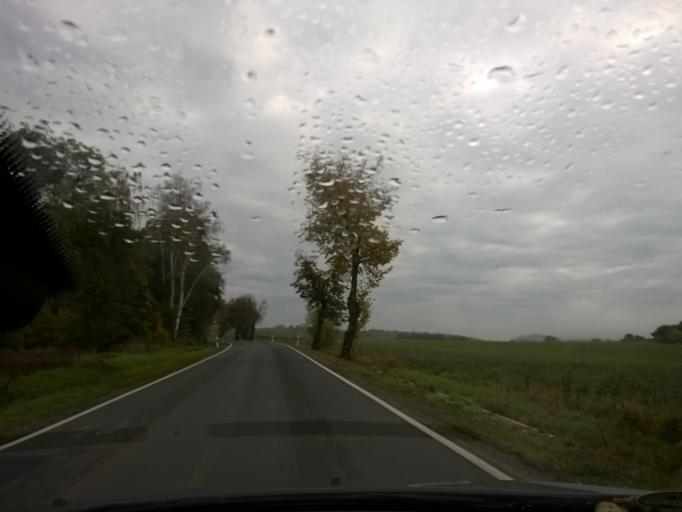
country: DE
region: Thuringia
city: Nordhausen
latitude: 51.5203
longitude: 10.8143
